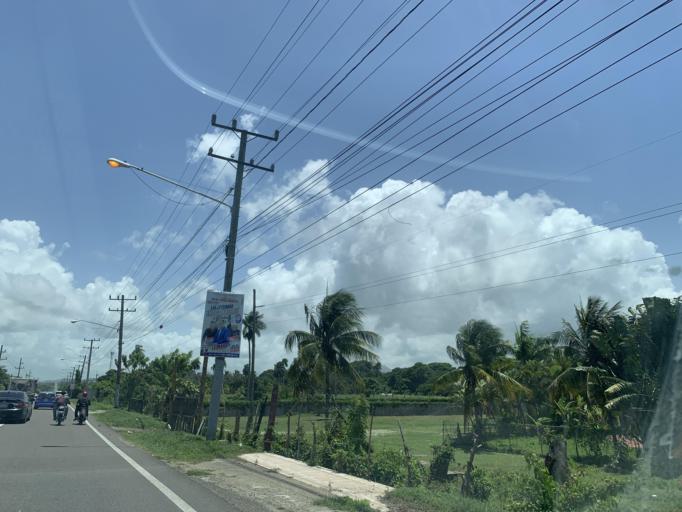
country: DO
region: Puerto Plata
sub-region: Puerto Plata
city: Puerto Plata
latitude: 19.7588
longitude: -70.6455
